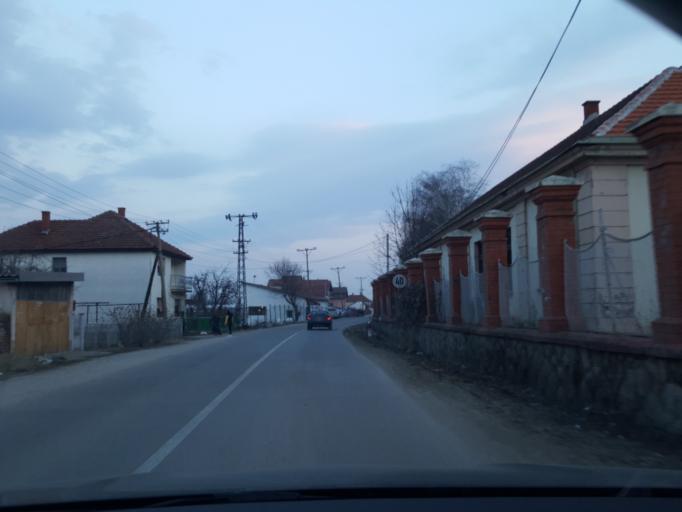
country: RS
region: Central Serbia
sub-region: Nisavski Okrug
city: Aleksinac
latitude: 43.5064
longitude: 21.6965
